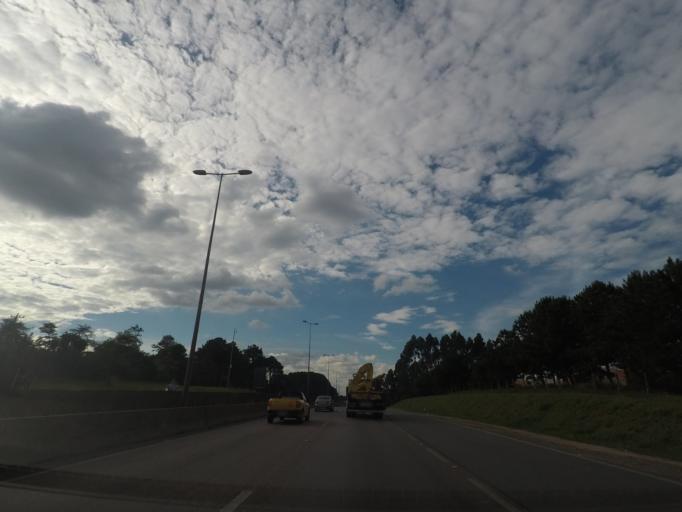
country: BR
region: Parana
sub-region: Araucaria
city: Araucaria
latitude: -25.5788
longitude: -49.3126
